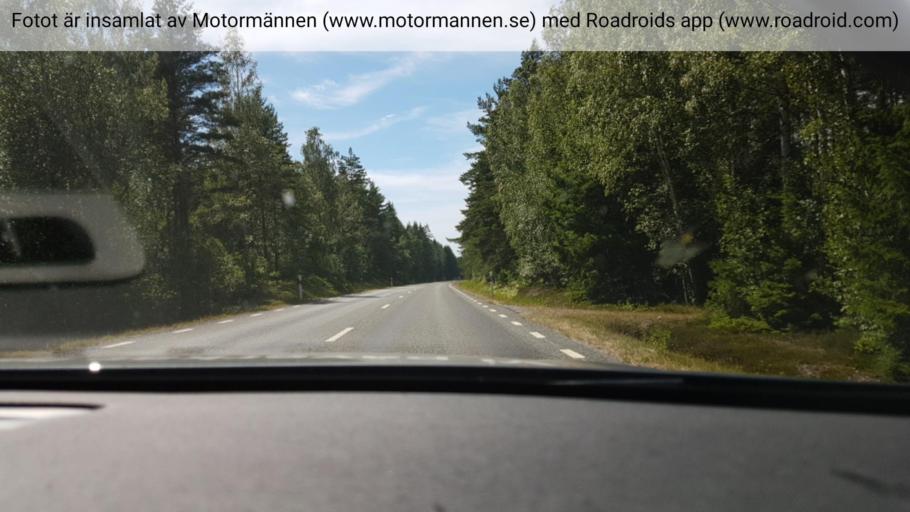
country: SE
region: Vaestra Goetaland
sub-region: Mariestads Kommun
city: Mariestad
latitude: 58.7051
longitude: 13.9724
